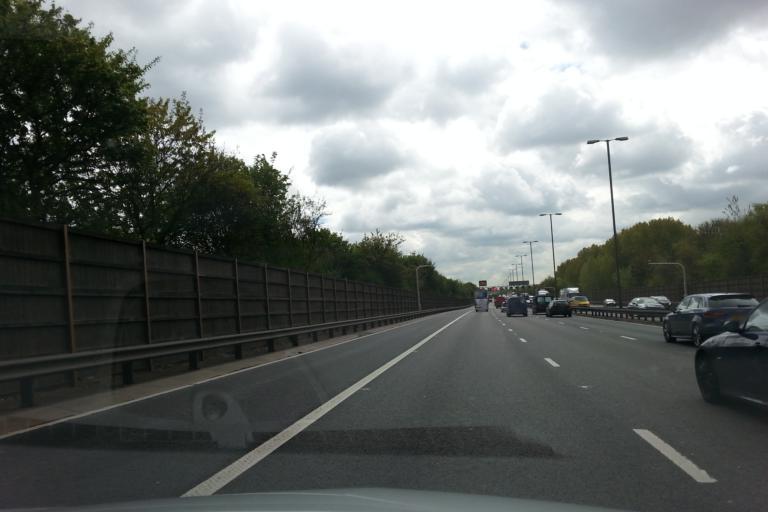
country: GB
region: England
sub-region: City and Borough of Birmingham
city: Hockley
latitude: 52.5455
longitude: -1.9168
